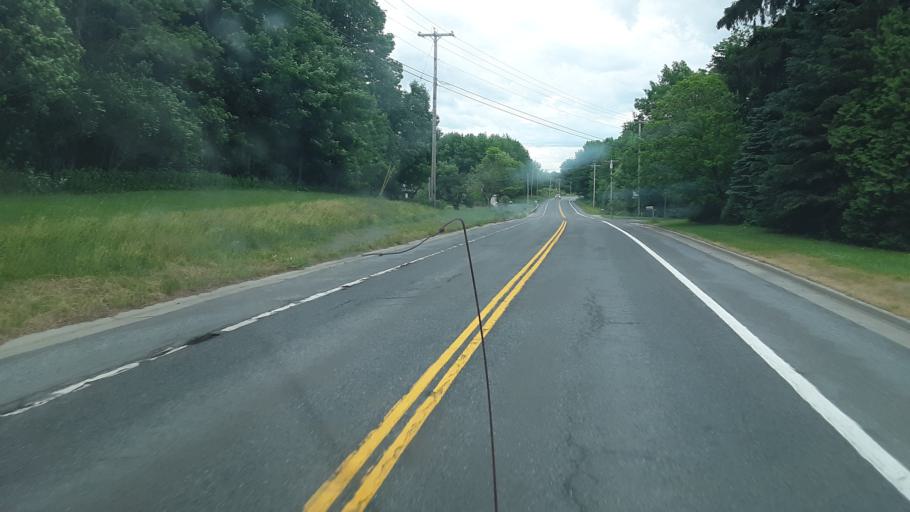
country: US
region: New York
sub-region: Oneida County
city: Rome
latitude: 43.3502
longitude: -75.4765
